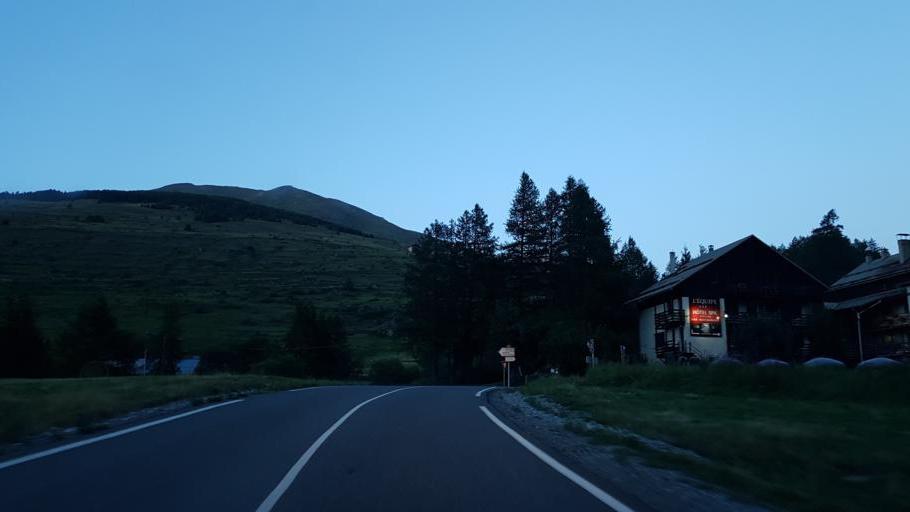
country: FR
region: Provence-Alpes-Cote d'Azur
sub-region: Departement des Hautes-Alpes
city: Guillestre
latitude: 44.7224
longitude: 6.8464
